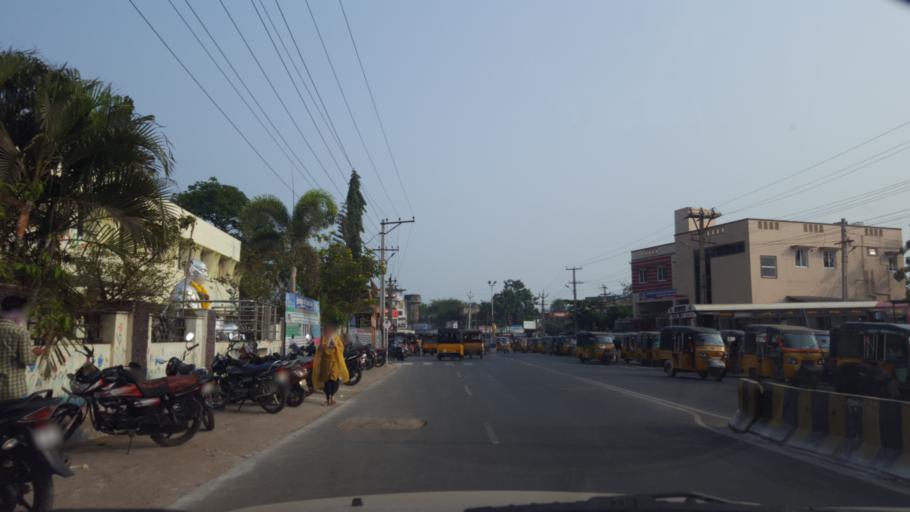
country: IN
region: Andhra Pradesh
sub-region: Srikakulam
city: Srikakulam
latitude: 18.2925
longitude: 83.8966
